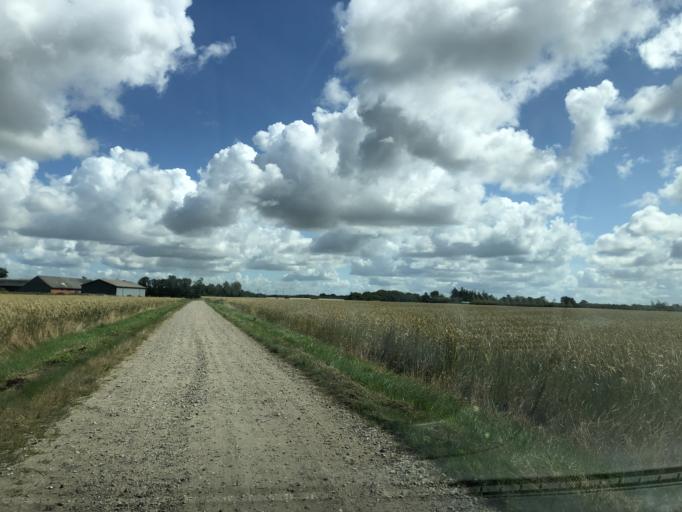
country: DK
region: Central Jutland
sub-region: Holstebro Kommune
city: Ulfborg
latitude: 56.3565
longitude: 8.3703
